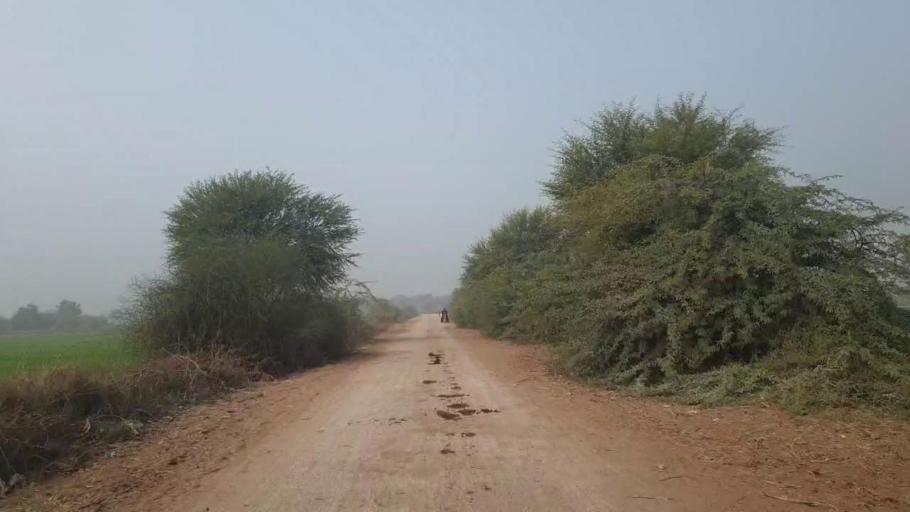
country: PK
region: Sindh
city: Bhit Shah
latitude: 25.8059
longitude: 68.5620
